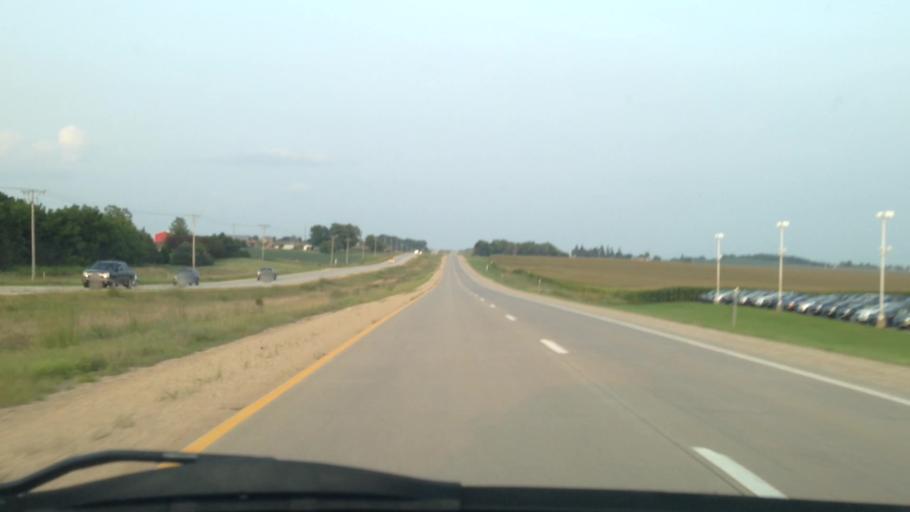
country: US
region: Iowa
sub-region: Benton County
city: Atkins
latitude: 41.9632
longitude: -91.9486
